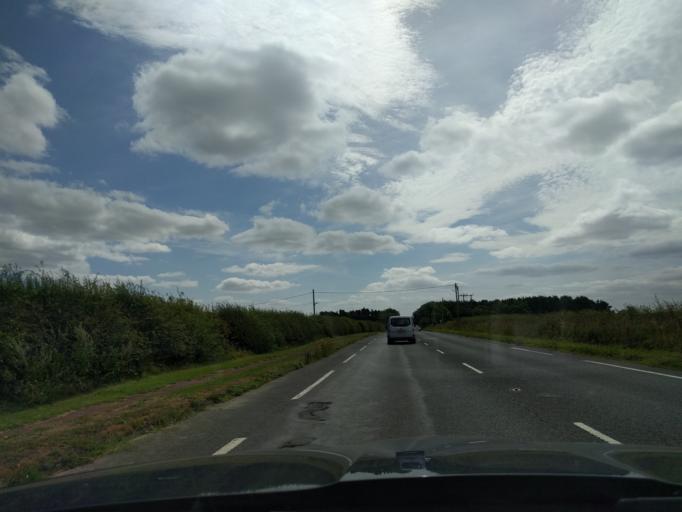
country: GB
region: England
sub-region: Northumberland
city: Stannington
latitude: 55.1235
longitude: -1.6708
